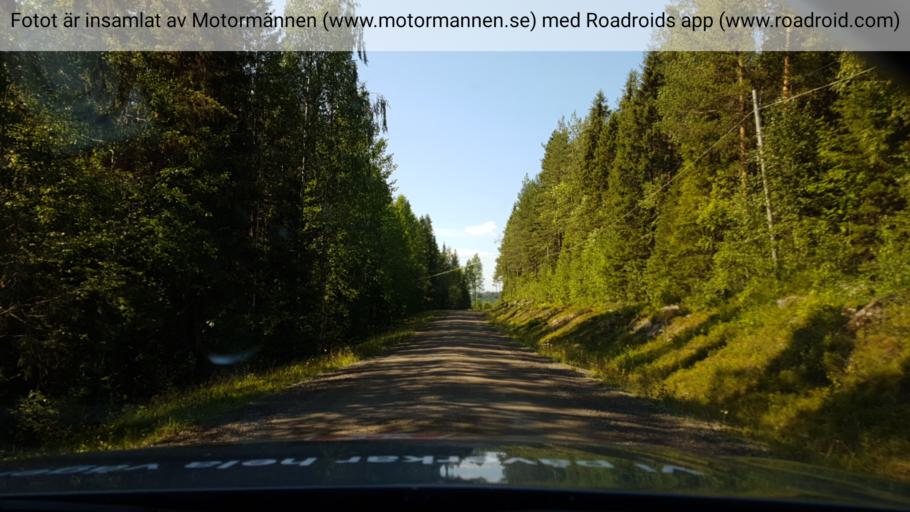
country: SE
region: Vaesterbotten
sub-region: Dorotea Kommun
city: Dorotea
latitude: 64.0855
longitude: 16.5408
